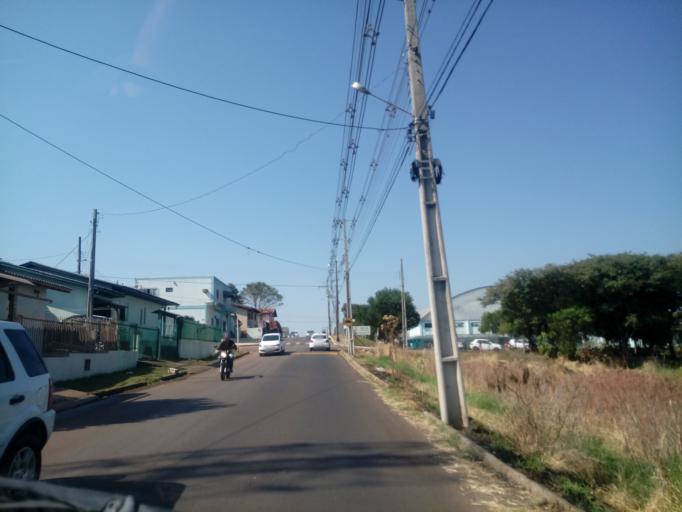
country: BR
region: Santa Catarina
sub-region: Chapeco
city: Chapeco
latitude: -27.0853
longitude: -52.6314
